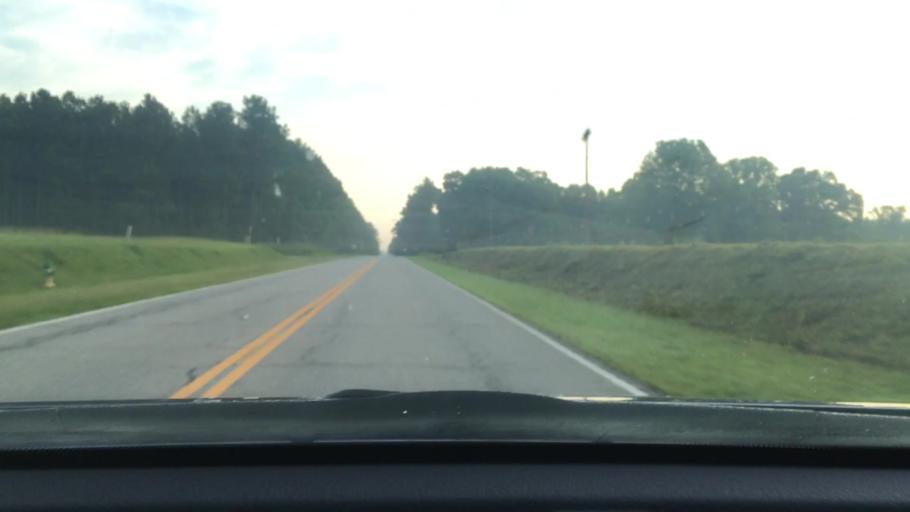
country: US
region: South Carolina
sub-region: Sumter County
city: East Sumter
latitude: 33.9724
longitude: -80.2998
